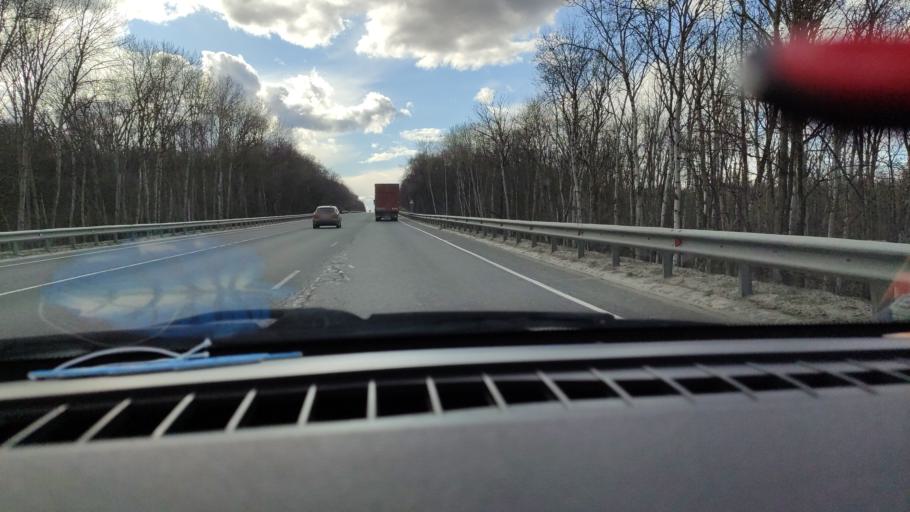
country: RU
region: Saratov
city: Vol'sk
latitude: 52.1074
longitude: 47.4095
